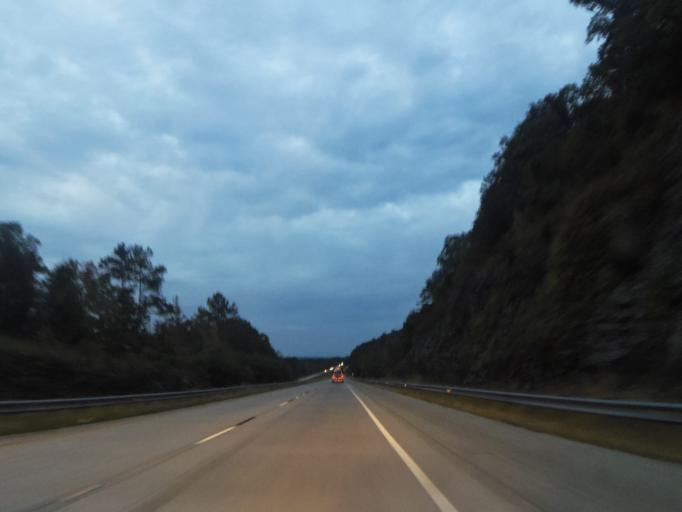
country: US
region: Alabama
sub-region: Etowah County
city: Whitesboro
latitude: 34.1416
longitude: -85.9904
